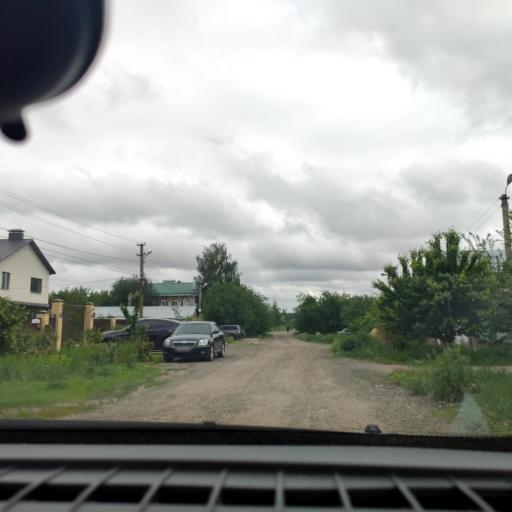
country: RU
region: Voronezj
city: Somovo
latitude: 51.6818
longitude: 39.3220
